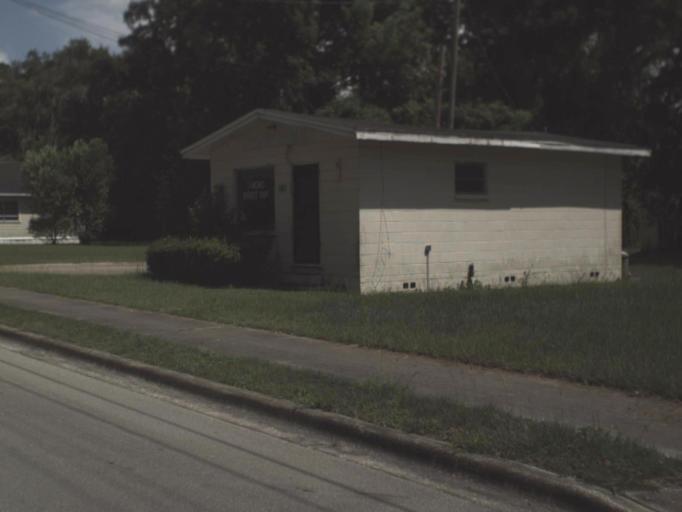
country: US
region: Florida
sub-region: Alachua County
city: High Springs
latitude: 29.8333
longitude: -82.6114
